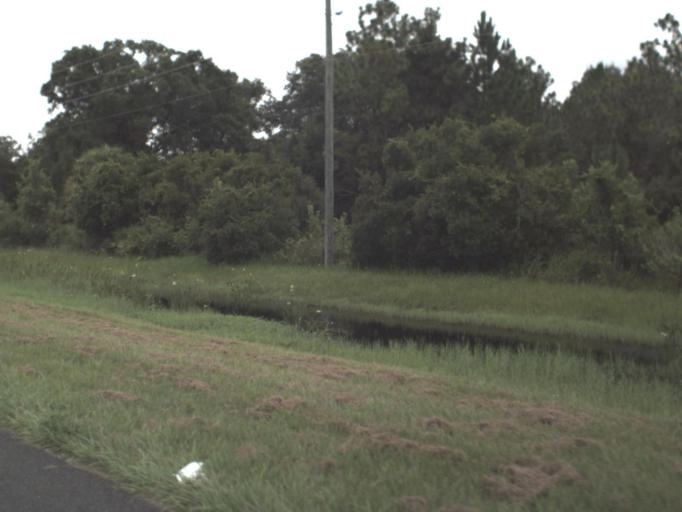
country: US
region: Florida
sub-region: Pasco County
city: Odessa
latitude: 28.1940
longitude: -82.5884
